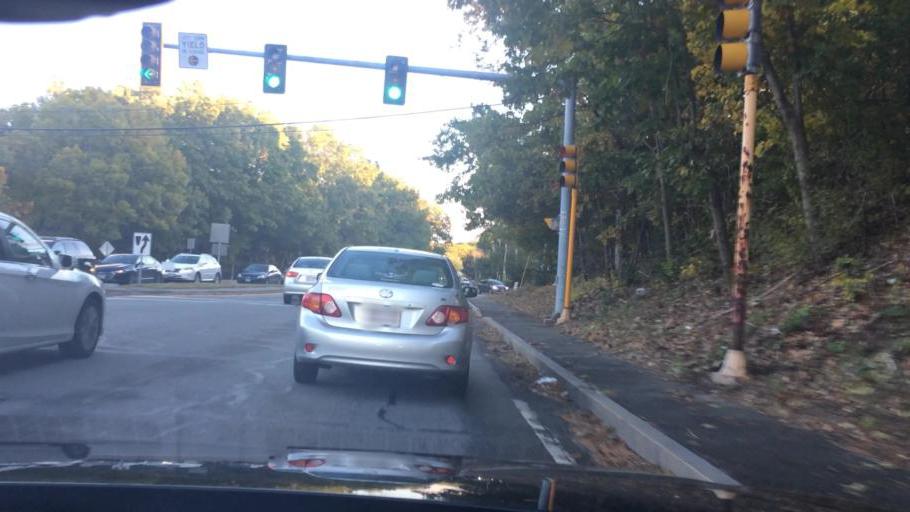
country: US
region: Massachusetts
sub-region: Middlesex County
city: Chelmsford
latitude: 42.6312
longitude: -71.3740
